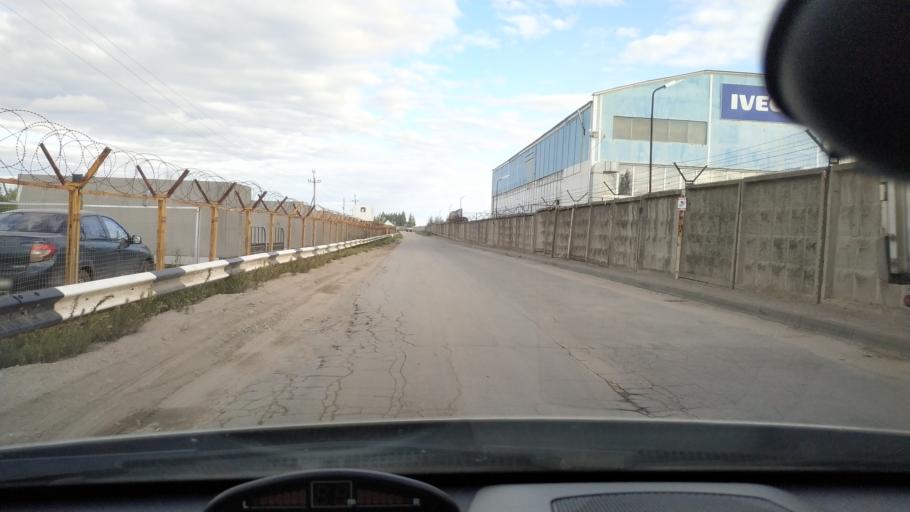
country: RU
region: Rjazan
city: Polyany
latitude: 54.5786
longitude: 39.8388
